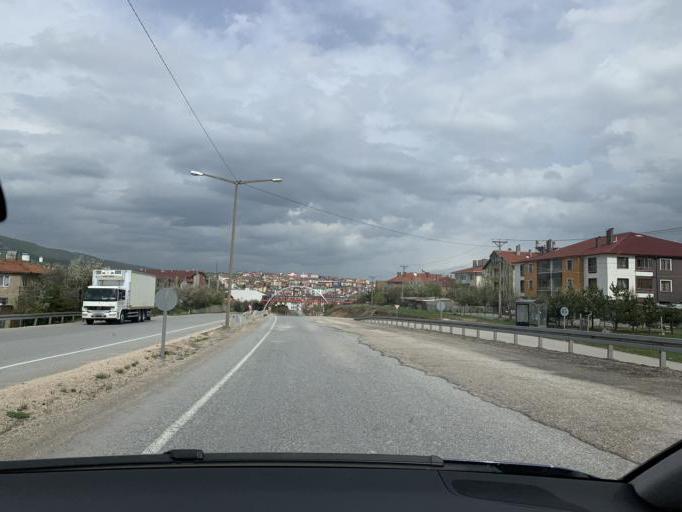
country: TR
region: Bolu
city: Gerede
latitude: 40.7962
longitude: 32.1956
